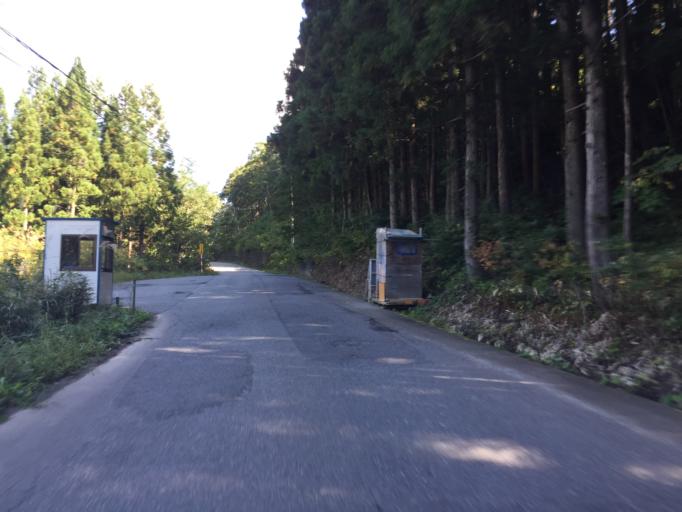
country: JP
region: Yamagata
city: Yonezawa
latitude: 37.8128
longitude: 140.2815
